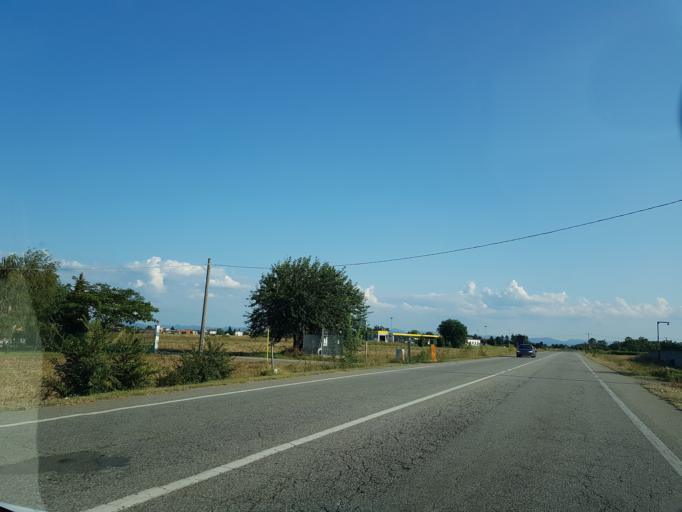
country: IT
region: Piedmont
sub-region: Provincia di Alessandria
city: Litta Parodi-Cascinagrossa
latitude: 44.8778
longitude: 8.6976
